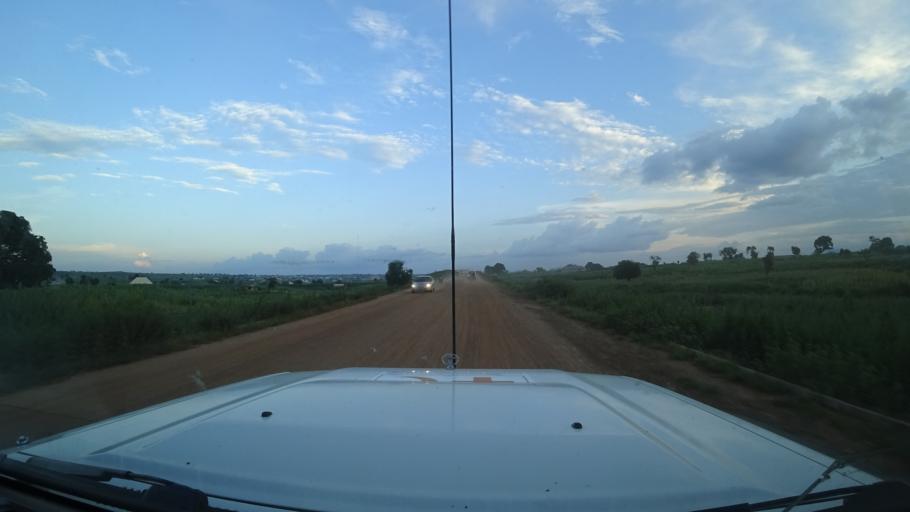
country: NG
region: Niger
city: Minna
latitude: 9.6542
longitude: 6.5761
